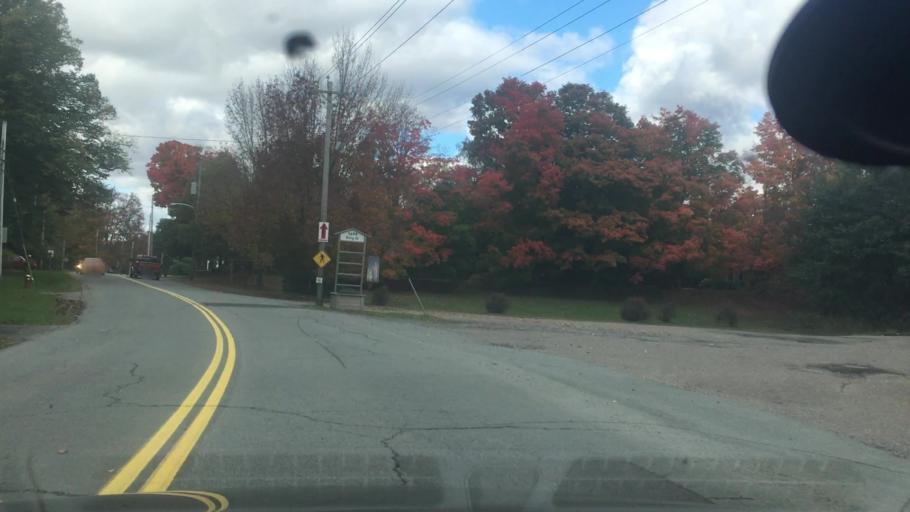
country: CA
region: Nova Scotia
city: Windsor
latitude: 44.9779
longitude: -64.1231
